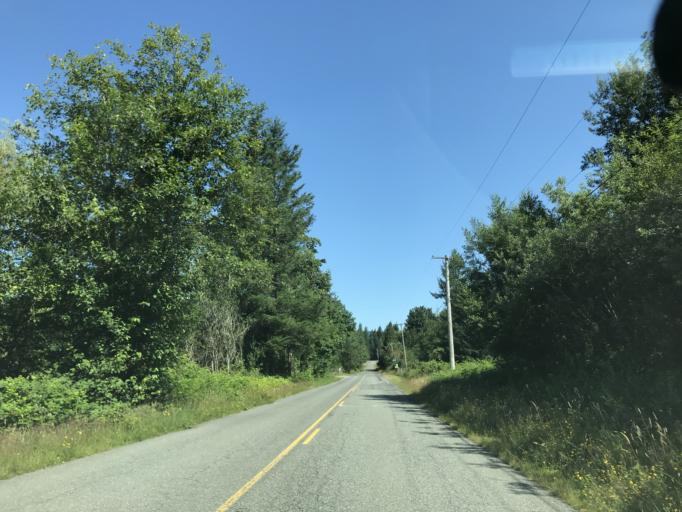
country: US
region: Washington
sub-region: King County
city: Ravensdale
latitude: 47.3649
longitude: -121.8802
